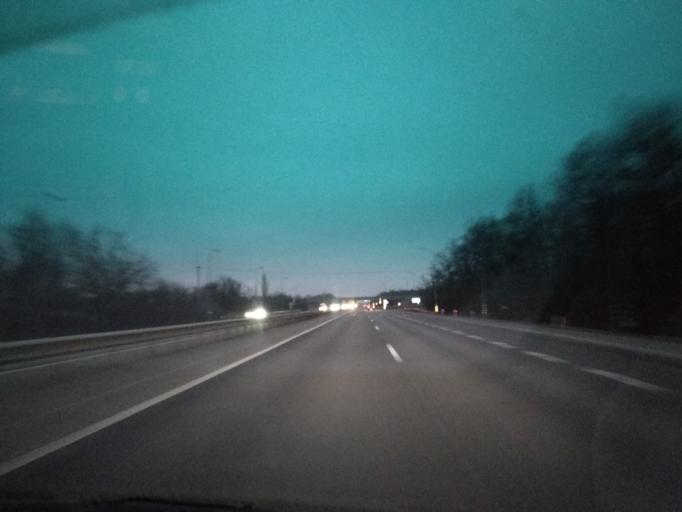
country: RU
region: Krasnodarskiy
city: Saratovskaya
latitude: 44.7706
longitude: 39.2319
